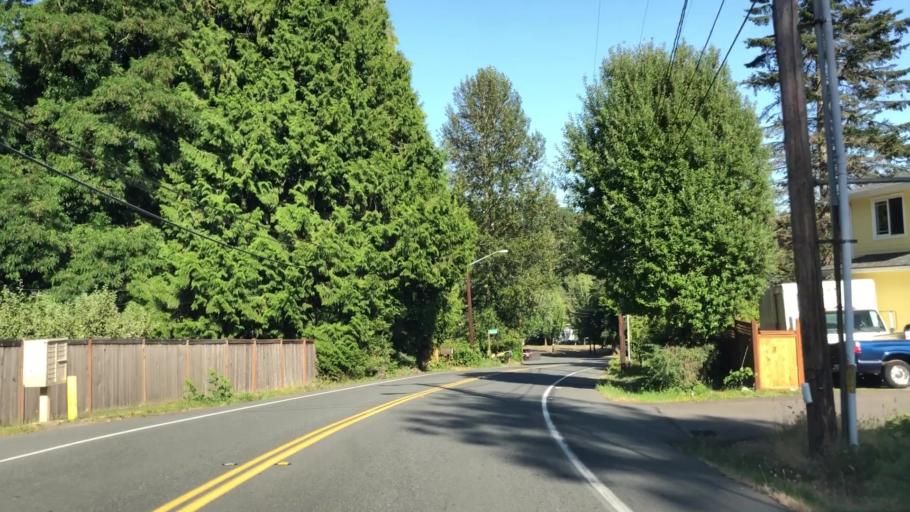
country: US
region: Washington
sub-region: Snohomish County
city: Brier
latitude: 47.7684
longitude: -122.2667
